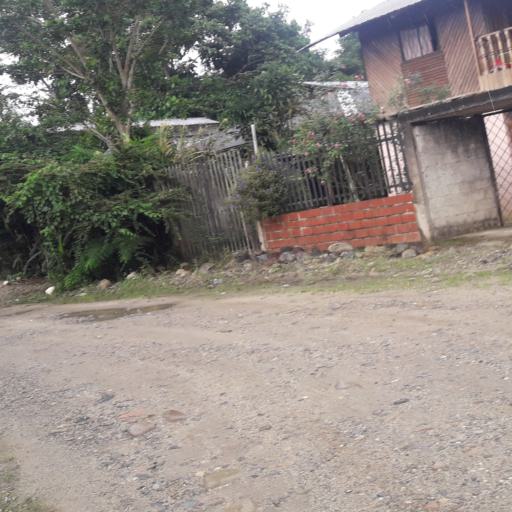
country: EC
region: Napo
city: Tena
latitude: -0.9911
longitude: -77.8104
